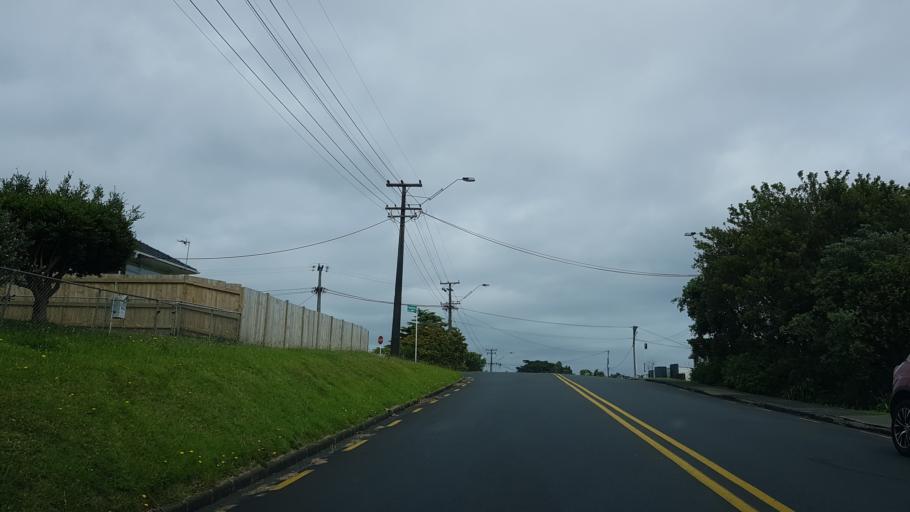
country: NZ
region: Auckland
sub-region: Auckland
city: North Shore
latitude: -36.8041
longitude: 174.7486
